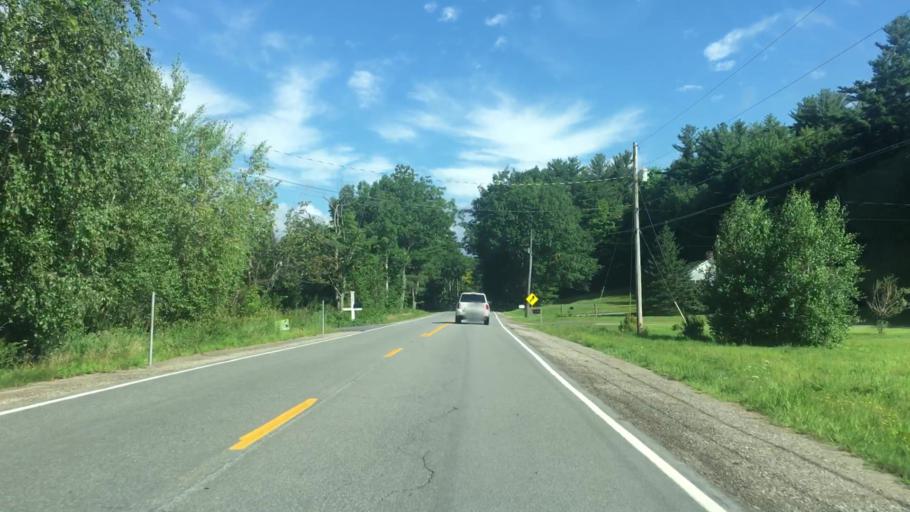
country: US
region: New Hampshire
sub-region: Belknap County
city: Gilford
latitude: 43.5409
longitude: -71.3489
